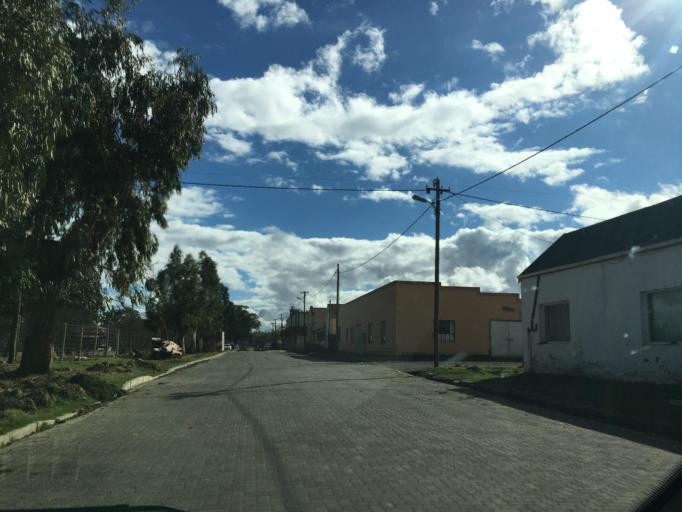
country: ZA
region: Eastern Cape
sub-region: Chris Hani District Municipality
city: Elliot
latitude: -31.3320
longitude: 27.8526
